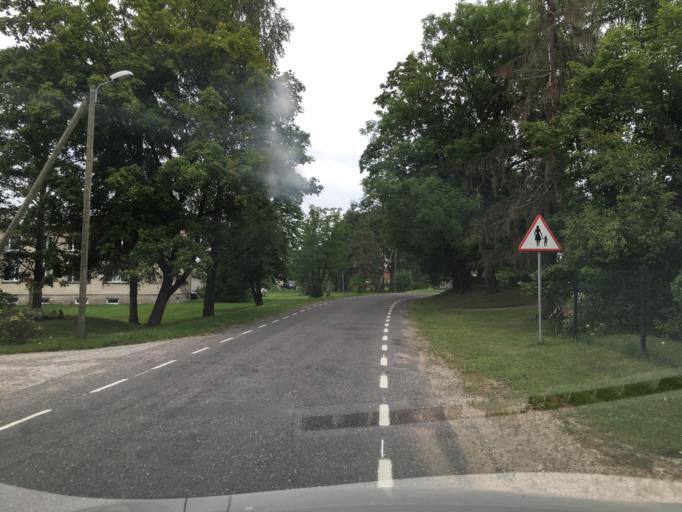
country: EE
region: Raplamaa
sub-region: Kehtna vald
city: Kehtna
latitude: 58.8602
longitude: 24.9997
